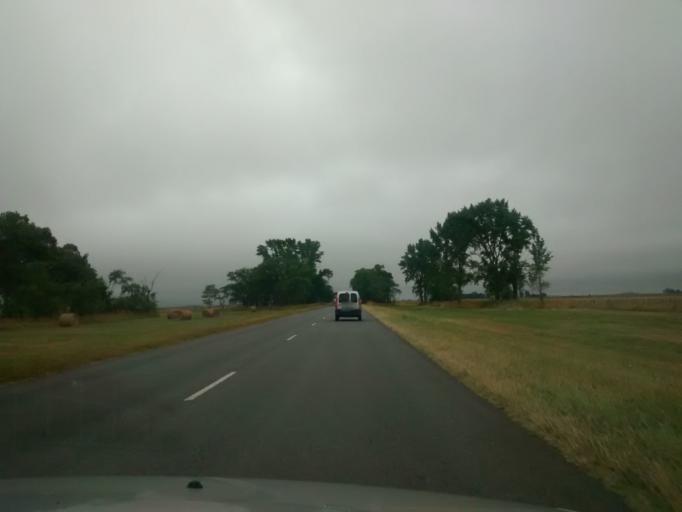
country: AR
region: Buenos Aires
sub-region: Partido de Ayacucho
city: Ayacucho
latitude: -37.2483
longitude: -58.4873
